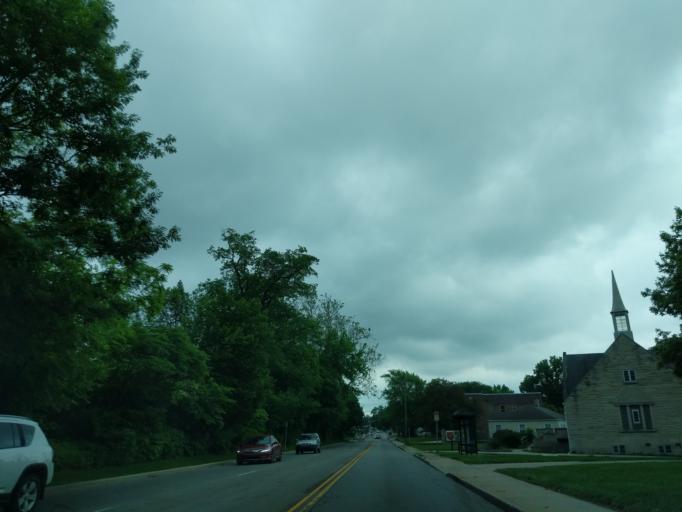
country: US
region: Indiana
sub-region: Delaware County
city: Muncie
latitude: 40.2035
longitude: -85.3937
